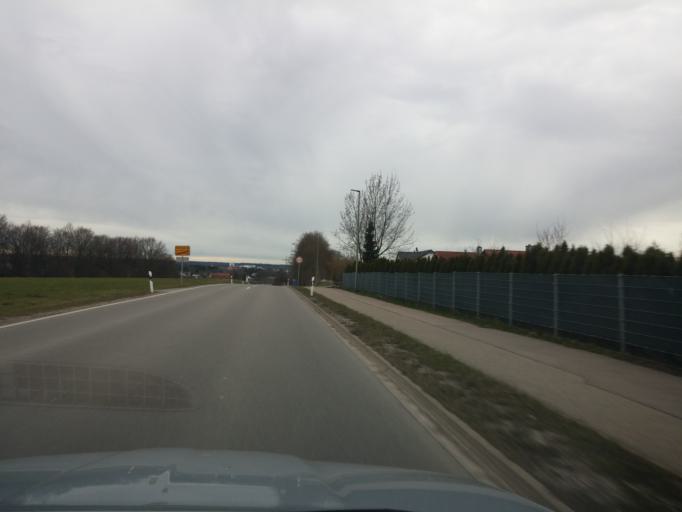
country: DE
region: Bavaria
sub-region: Swabia
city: Trunkelsberg
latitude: 48.0000
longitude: 10.2089
